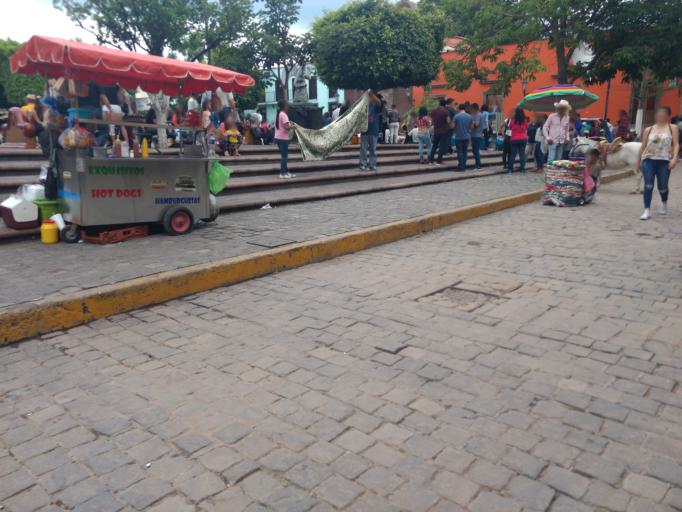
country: MX
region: Jalisco
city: Tequila
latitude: 20.8846
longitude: -103.8390
